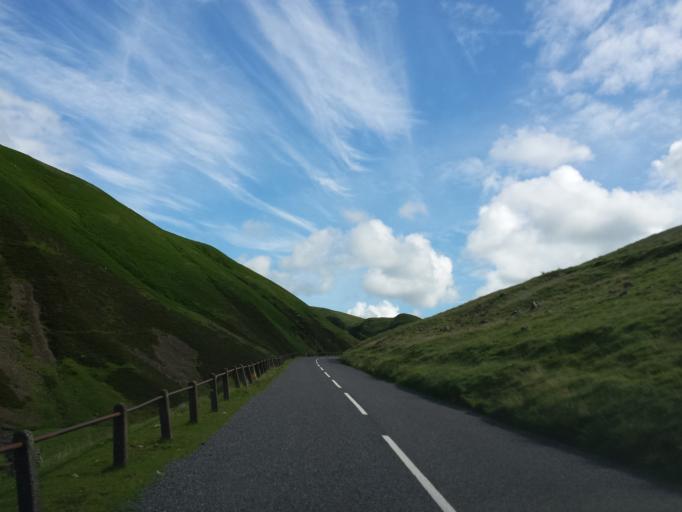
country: GB
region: Scotland
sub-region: Dumfries and Galloway
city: Moffat
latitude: 55.4226
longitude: -3.2770
